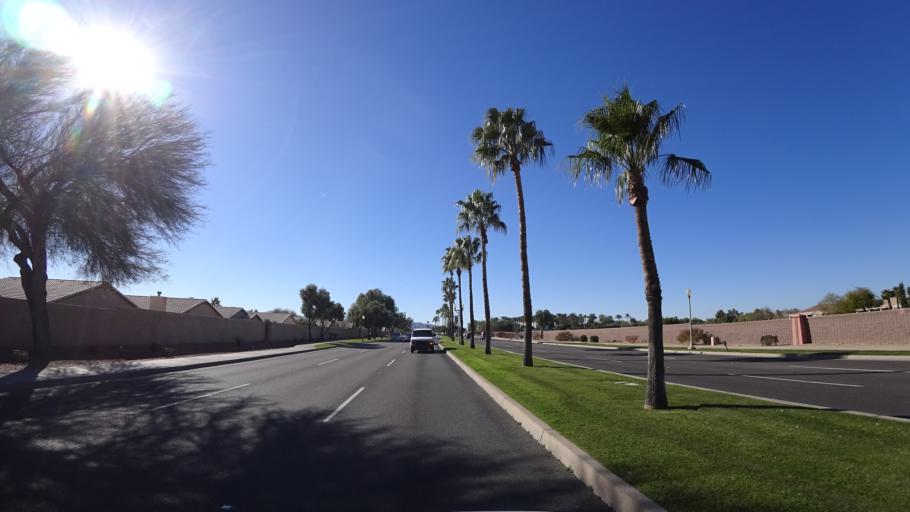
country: US
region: Arizona
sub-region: Maricopa County
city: Sun City West
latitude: 33.6387
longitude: -112.4013
